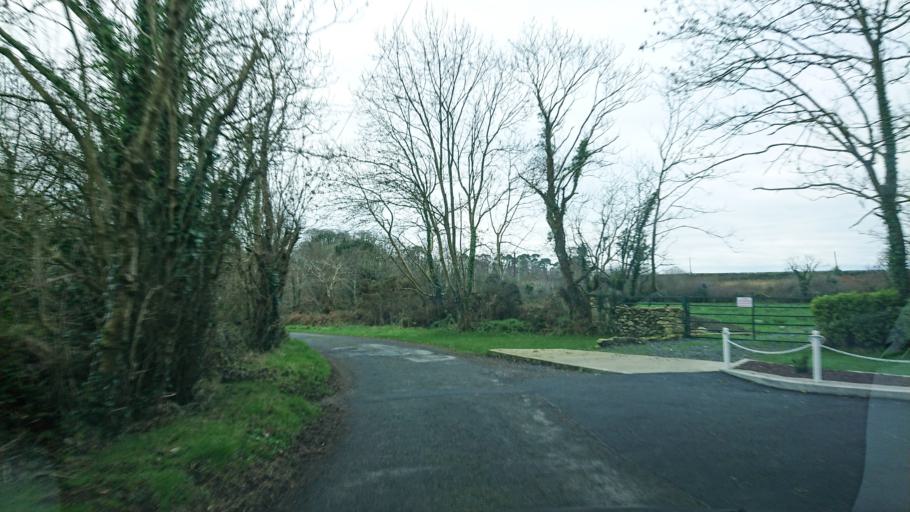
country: IE
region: Leinster
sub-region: Kilkenny
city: Mooncoin
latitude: 52.2118
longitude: -7.2709
